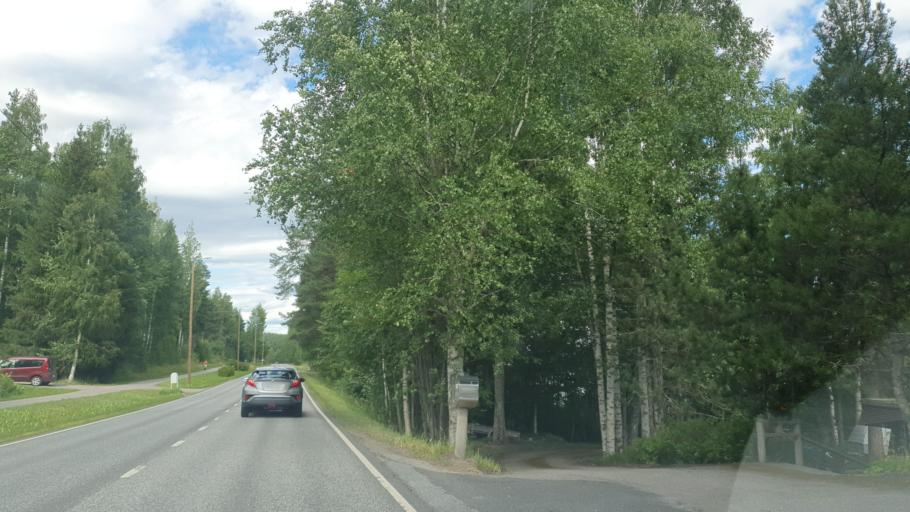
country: FI
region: Central Finland
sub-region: Jyvaeskylae
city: Saeynaetsalo
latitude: 62.1482
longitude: 25.7509
